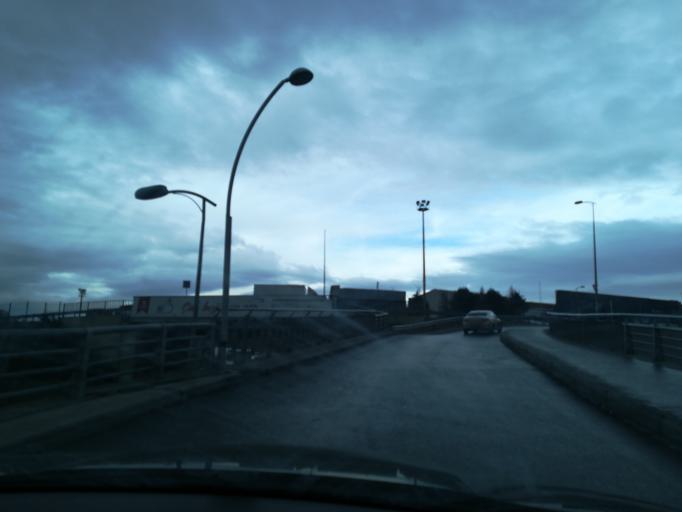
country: TR
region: Istanbul
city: Mahmutbey
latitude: 41.0625
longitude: 28.8038
